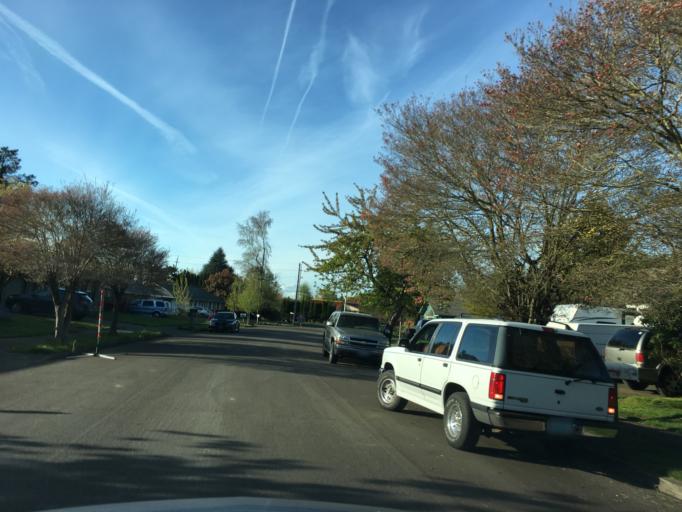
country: US
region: Oregon
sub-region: Multnomah County
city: Lents
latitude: 45.5528
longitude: -122.5251
